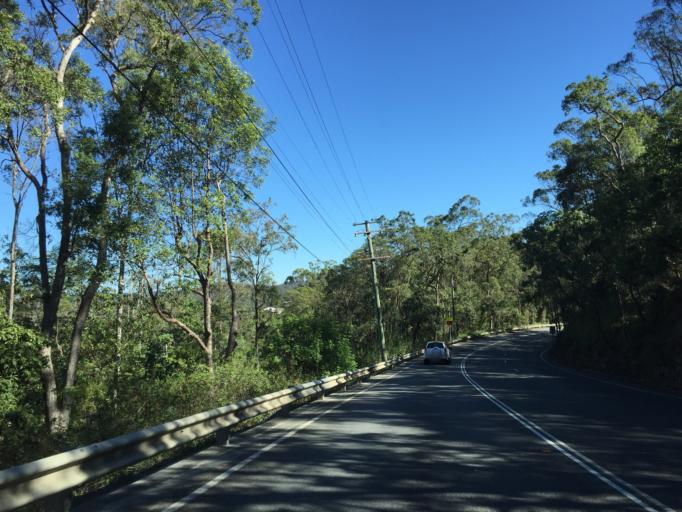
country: AU
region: Queensland
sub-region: Moreton Bay
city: Ferny Hills
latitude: -27.4281
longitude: 152.9472
